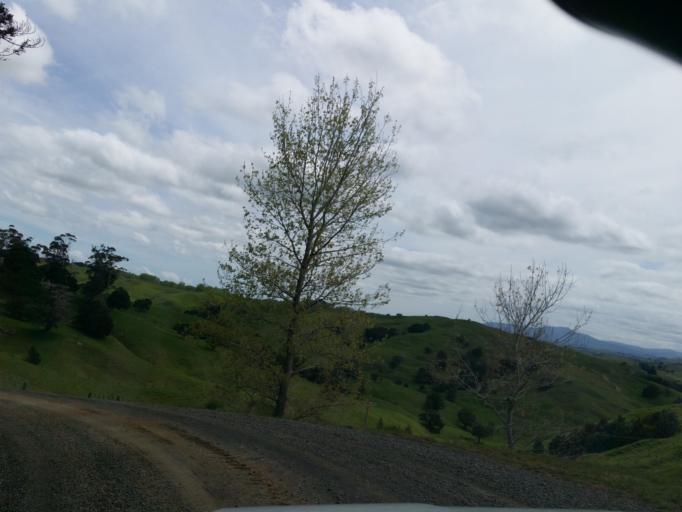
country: NZ
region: Northland
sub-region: Kaipara District
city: Dargaville
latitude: -35.9086
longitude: 174.0498
